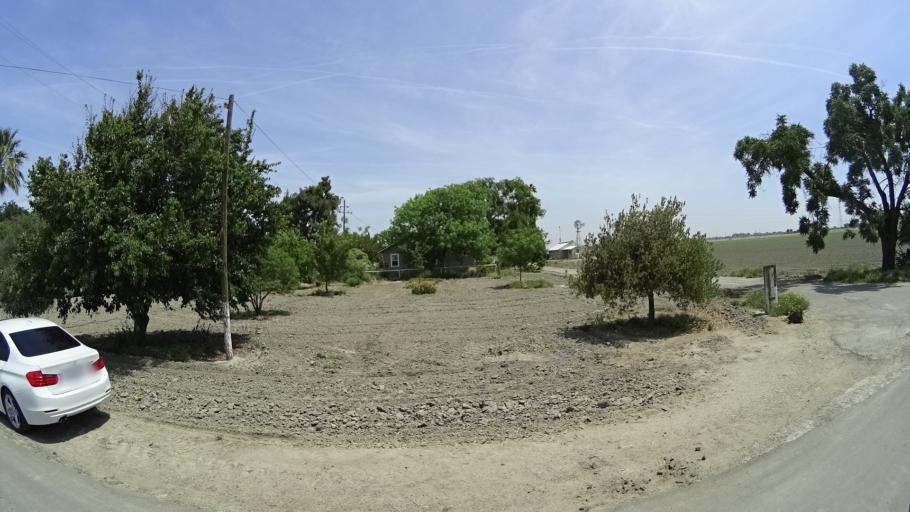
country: US
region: California
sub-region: Fresno County
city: Riverdale
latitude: 36.4043
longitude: -119.8955
